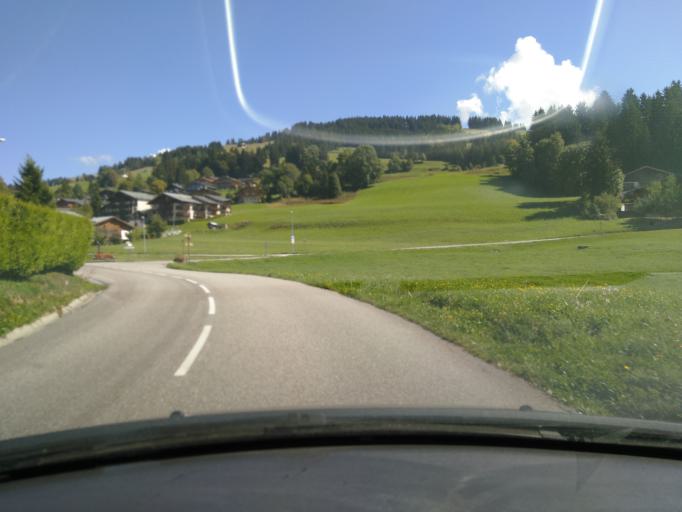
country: FR
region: Rhone-Alpes
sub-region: Departement de la Haute-Savoie
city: Praz-sur-Arly
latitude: 45.7901
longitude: 6.4996
